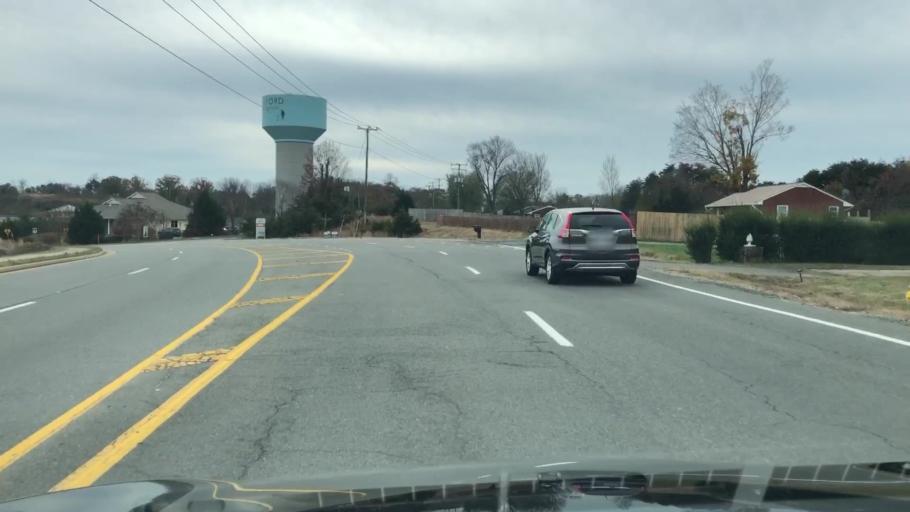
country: US
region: Virginia
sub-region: Stafford County
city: Falmouth
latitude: 38.3577
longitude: -77.5242
